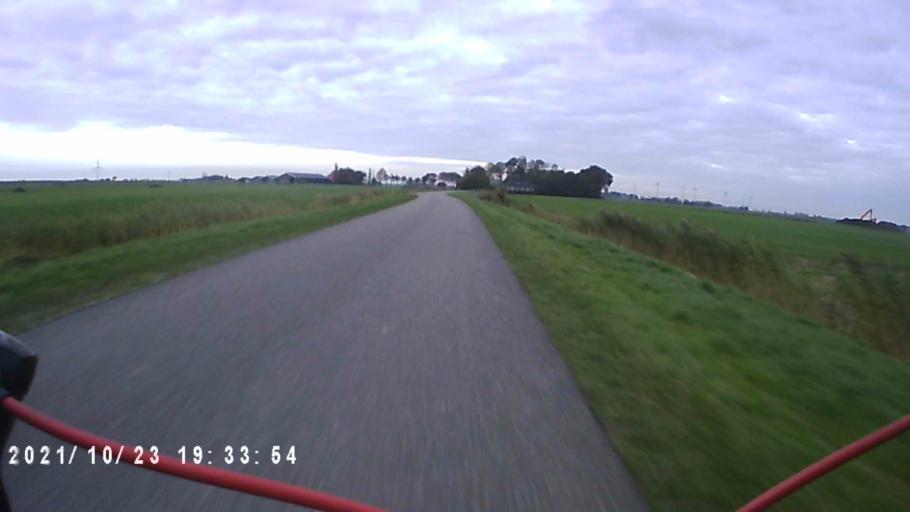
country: NL
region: Friesland
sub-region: Sudwest Fryslan
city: Makkum
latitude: 53.0891
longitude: 5.3919
